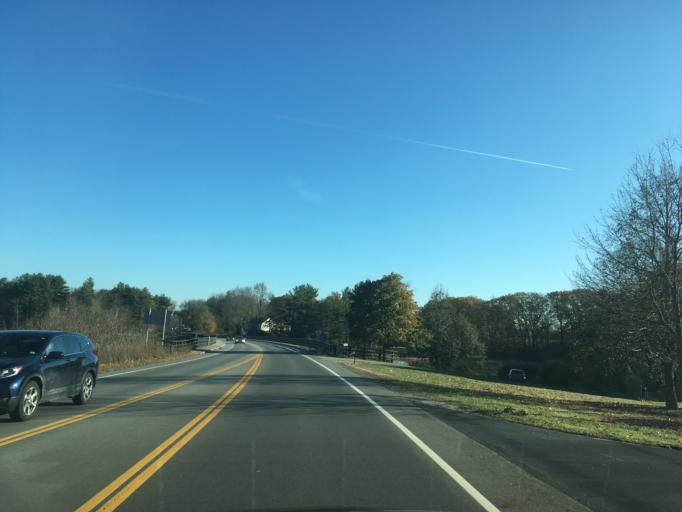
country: US
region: New Hampshire
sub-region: Rockingham County
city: Stratham Station
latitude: 43.0406
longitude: -70.9295
